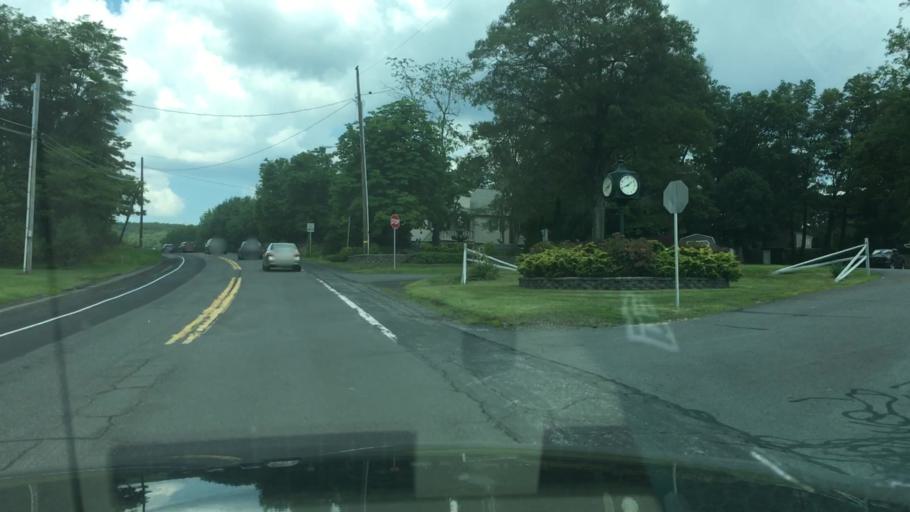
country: US
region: Pennsylvania
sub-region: Schuylkill County
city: Minersville
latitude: 40.7061
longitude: -76.3288
